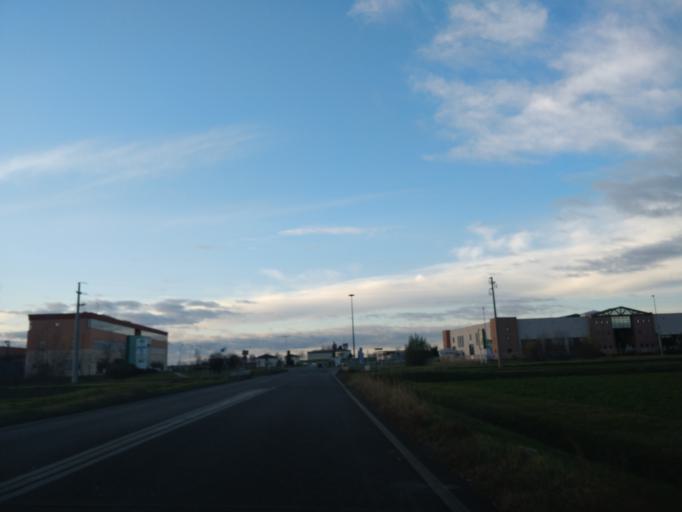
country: IT
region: Emilia-Romagna
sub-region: Provincia di Ferrara
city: Cento
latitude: 44.7451
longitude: 11.2800
